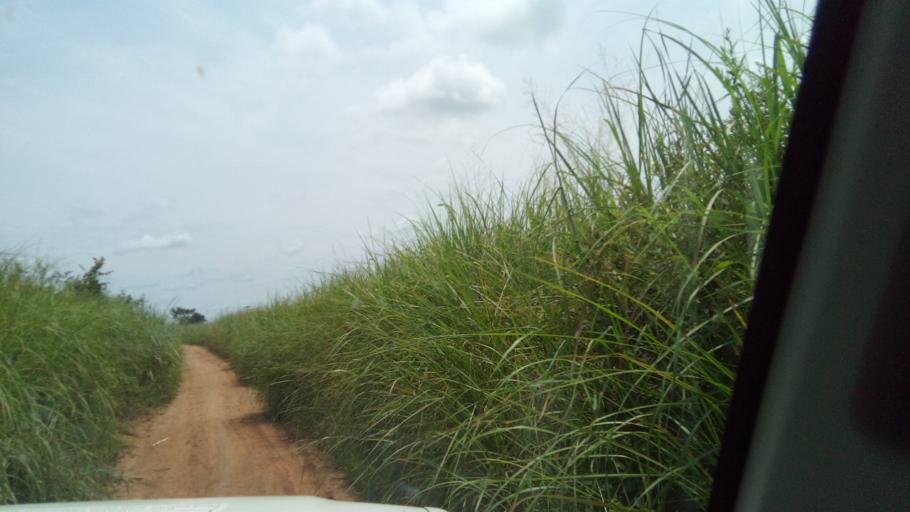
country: AO
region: Zaire
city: Mbanza Congo
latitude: -5.8004
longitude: 13.9960
